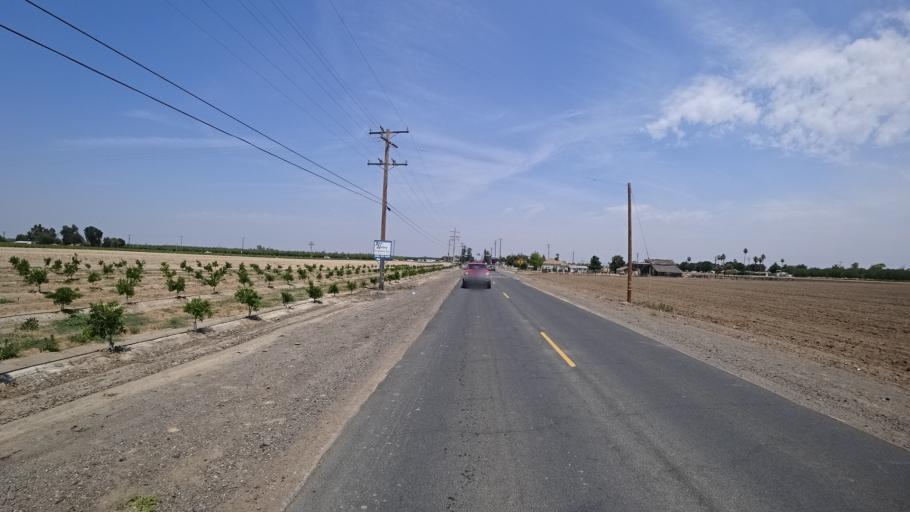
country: US
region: California
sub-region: Kings County
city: Armona
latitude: 36.3260
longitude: -119.6911
